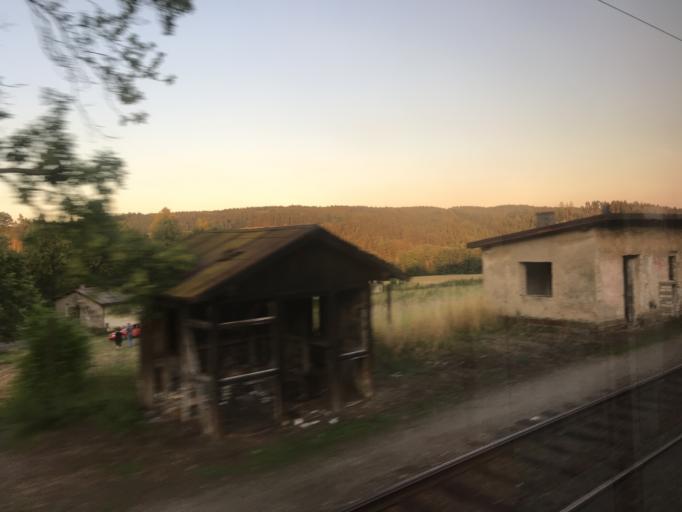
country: CZ
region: Central Bohemia
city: Votice
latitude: 49.6025
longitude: 14.5838
